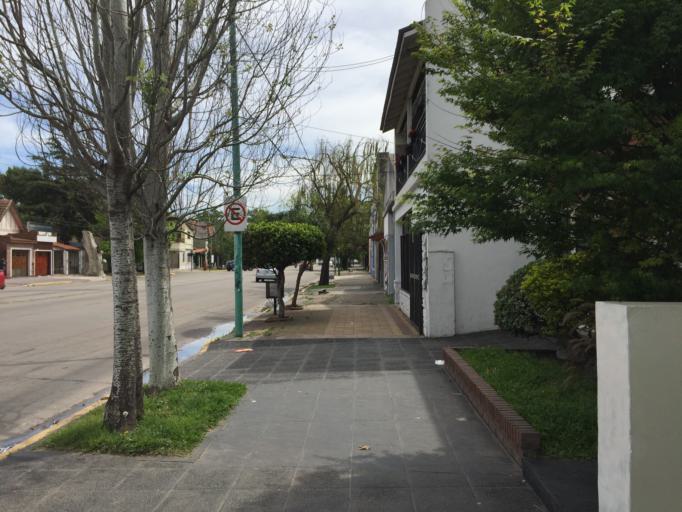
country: AR
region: Buenos Aires
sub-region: Partido de Lomas de Zamora
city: Lomas de Zamora
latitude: -34.7382
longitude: -58.3922
